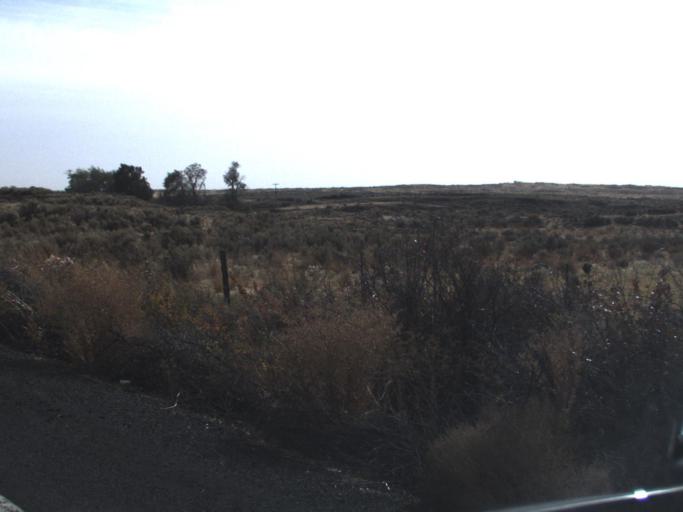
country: US
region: Washington
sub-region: Adams County
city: Ritzville
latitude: 47.4175
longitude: -118.6863
